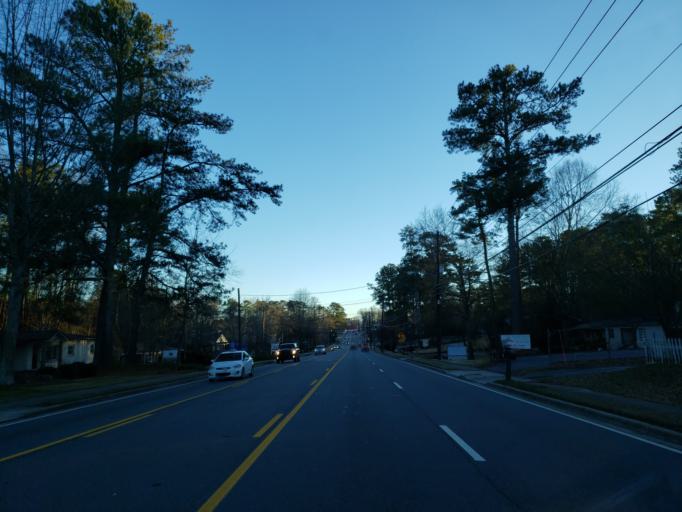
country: US
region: Georgia
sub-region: Fulton County
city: Alpharetta
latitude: 34.0840
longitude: -84.2950
